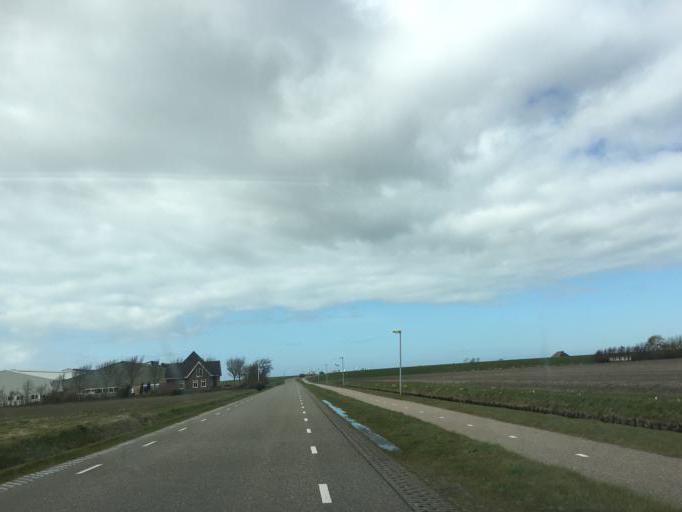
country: NL
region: North Holland
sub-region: Gemeente Schagen
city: Schagen
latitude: 52.8433
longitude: 4.7446
